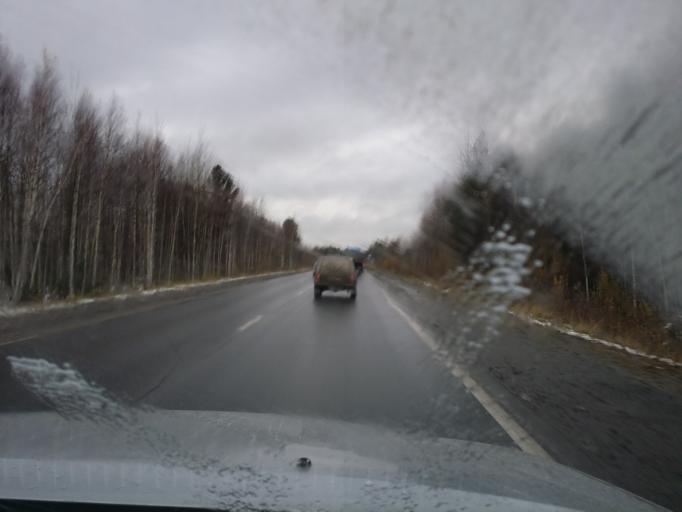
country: RU
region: Khanty-Mansiyskiy Avtonomnyy Okrug
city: Megion
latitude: 61.1289
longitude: 75.7885
